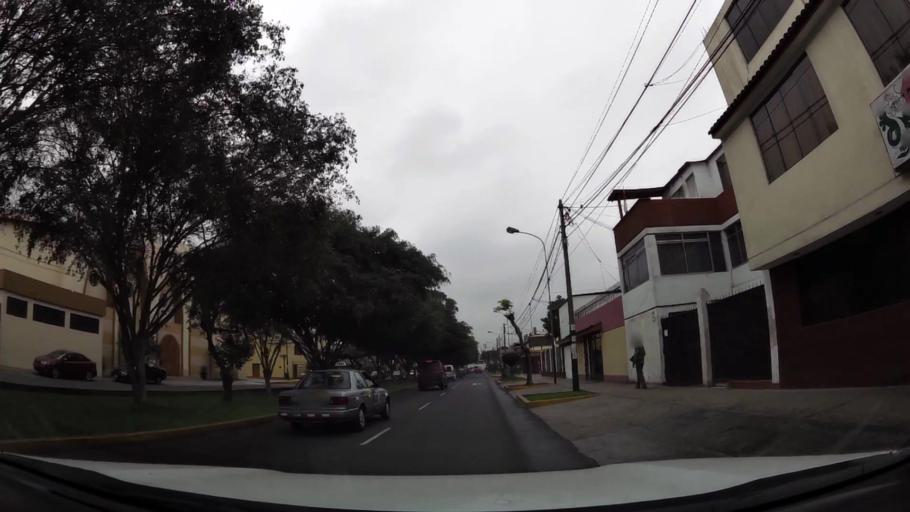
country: PE
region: Lima
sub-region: Lima
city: Surco
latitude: -12.1384
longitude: -77.0016
